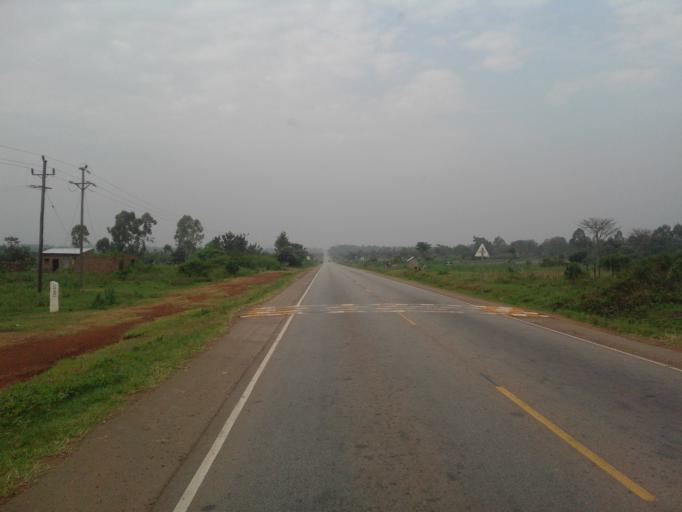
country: UG
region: Eastern Region
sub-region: Tororo District
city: Tororo
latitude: 0.6239
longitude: 34.0966
